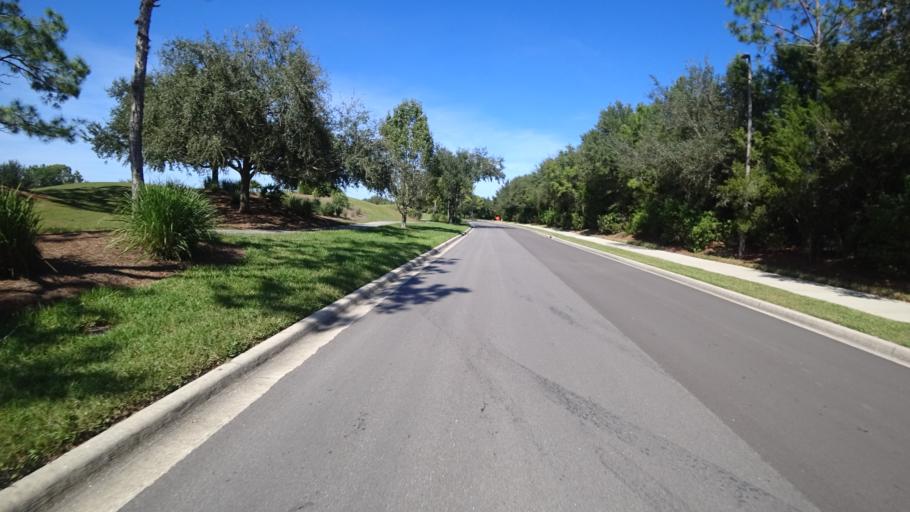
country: US
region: Florida
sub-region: Sarasota County
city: The Meadows
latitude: 27.4110
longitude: -82.4159
